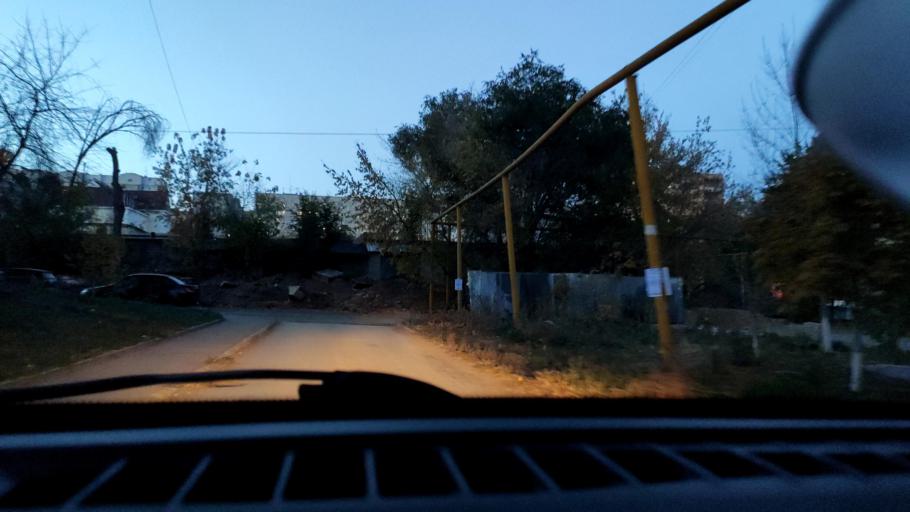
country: RU
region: Samara
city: Samara
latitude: 53.2045
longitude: 50.2233
